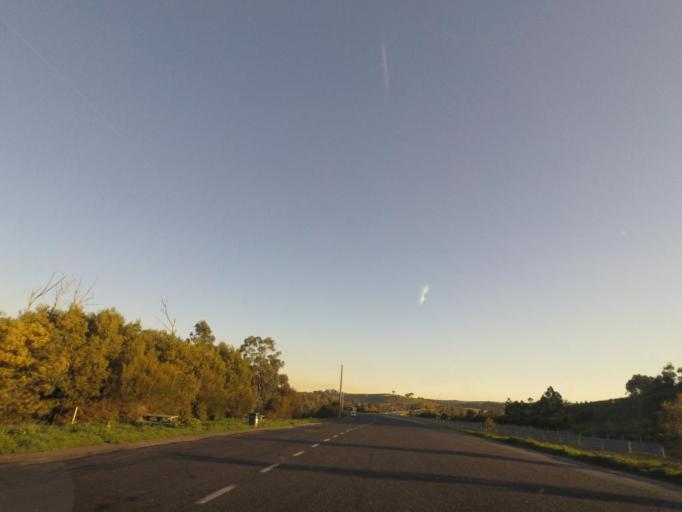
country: AU
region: Victoria
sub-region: Whittlesea
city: Whittlesea
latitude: -37.3285
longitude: 145.0311
